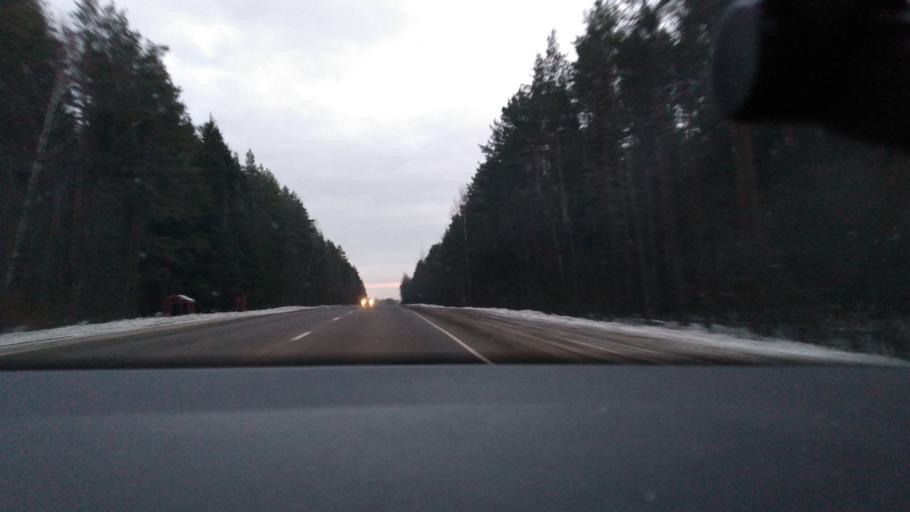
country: RU
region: Moskovskaya
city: Yegor'yevsk
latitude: 55.4297
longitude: 39.0312
